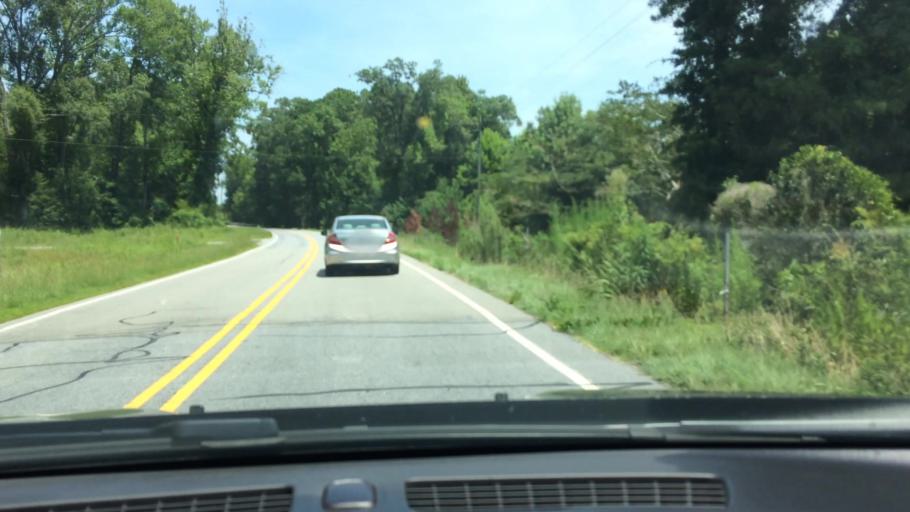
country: US
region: North Carolina
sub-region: Beaufort County
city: Washington
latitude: 35.5861
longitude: -77.1668
